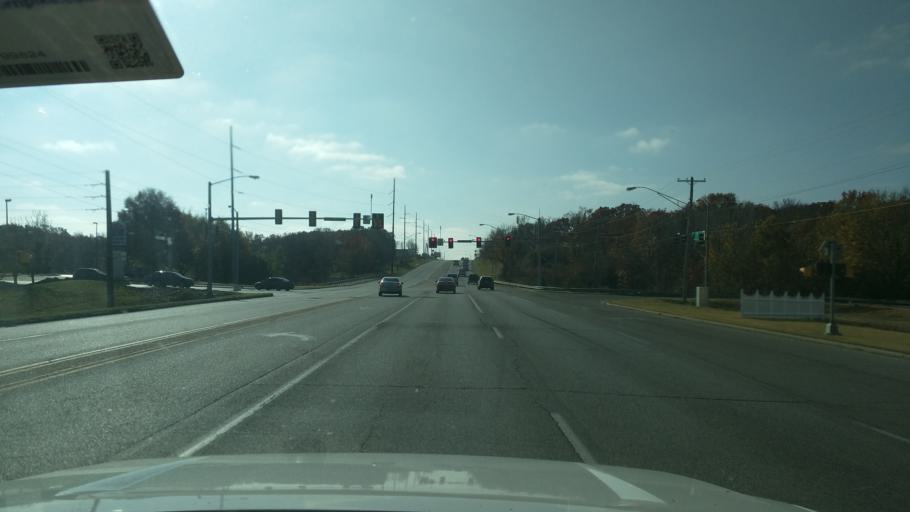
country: US
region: Oklahoma
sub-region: Washington County
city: Bartlesville
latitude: 36.7409
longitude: -95.9354
